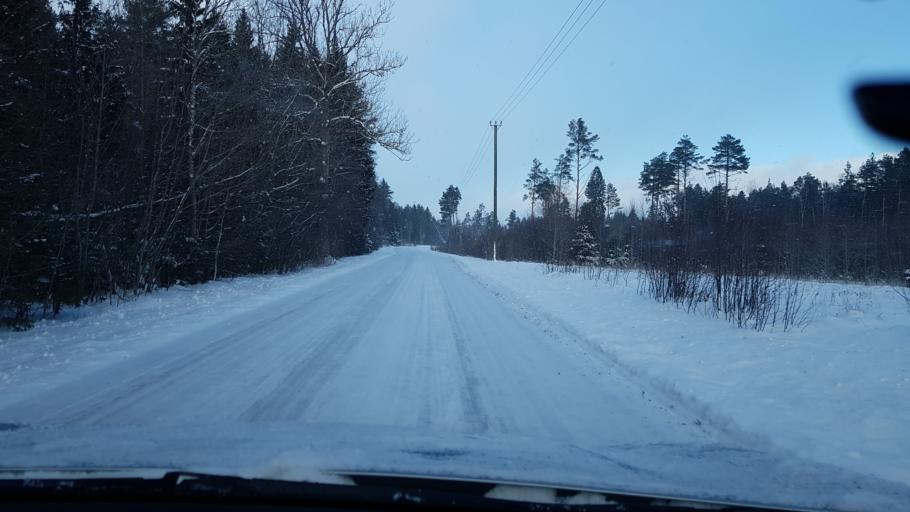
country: EE
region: Harju
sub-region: Nissi vald
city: Turba
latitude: 59.1896
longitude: 24.1397
